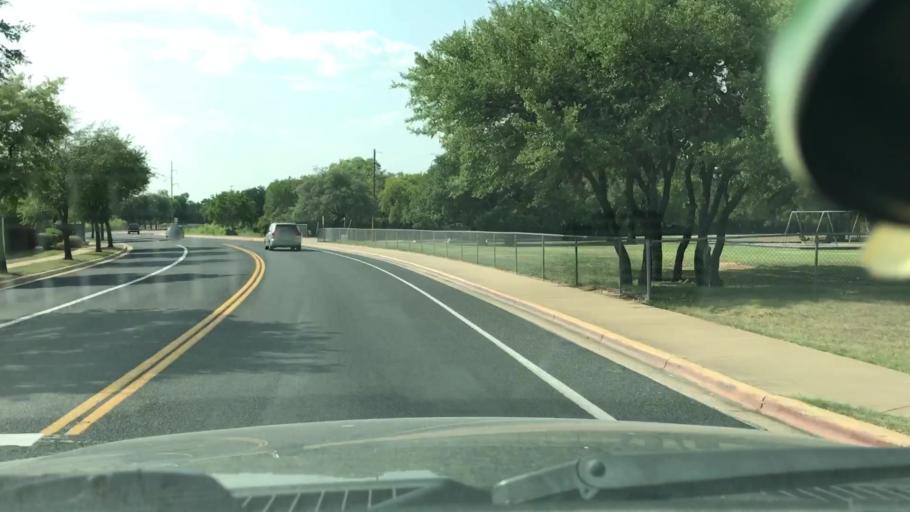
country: US
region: Texas
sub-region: Williamson County
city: Cedar Park
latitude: 30.5398
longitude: -97.8326
